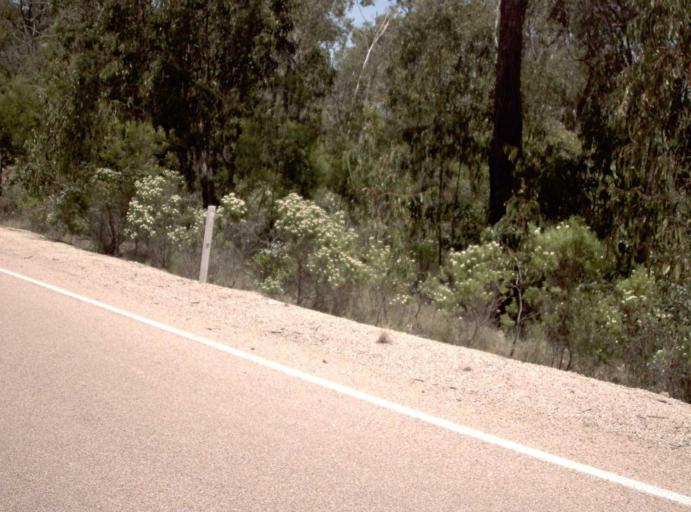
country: AU
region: Victoria
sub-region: East Gippsland
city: Lakes Entrance
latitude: -37.6111
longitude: 147.8810
